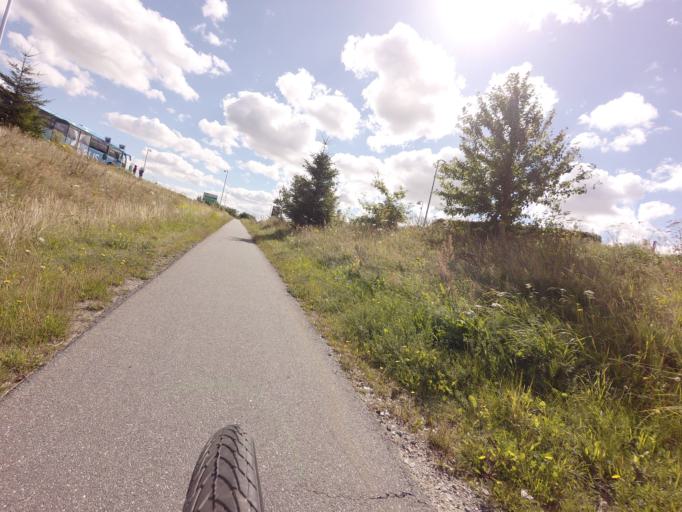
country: DK
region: Central Jutland
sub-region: Horsens Kommune
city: Horsens
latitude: 55.8865
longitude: 9.7873
